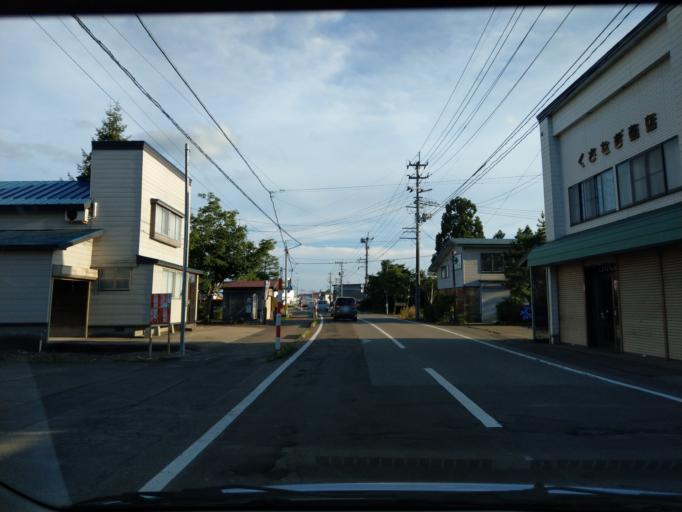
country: JP
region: Akita
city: Omagari
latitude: 39.4433
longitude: 140.5661
